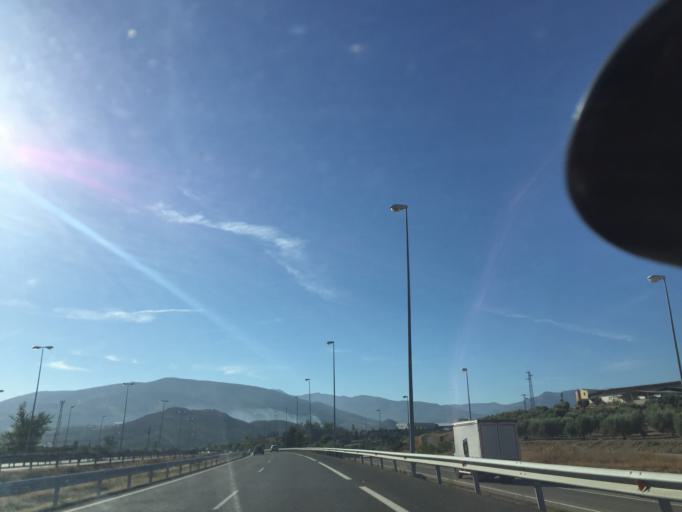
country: ES
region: Andalusia
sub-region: Provincia de Jaen
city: Jaen
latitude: 37.7873
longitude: -3.7570
